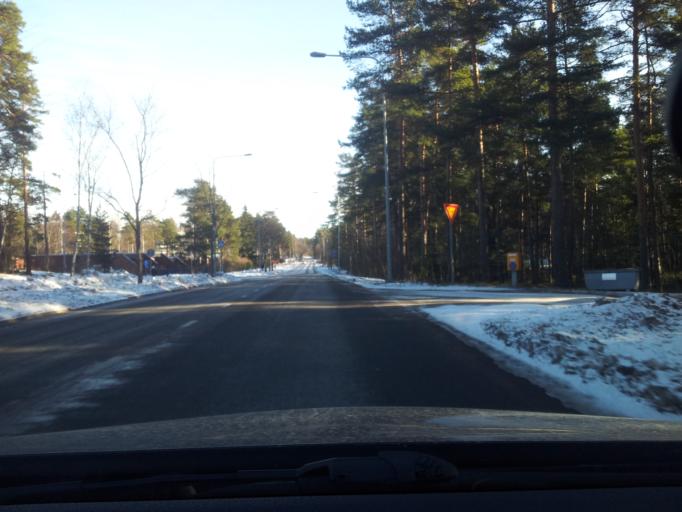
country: FI
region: Uusimaa
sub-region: Helsinki
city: Koukkuniemi
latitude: 60.1503
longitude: 24.7508
